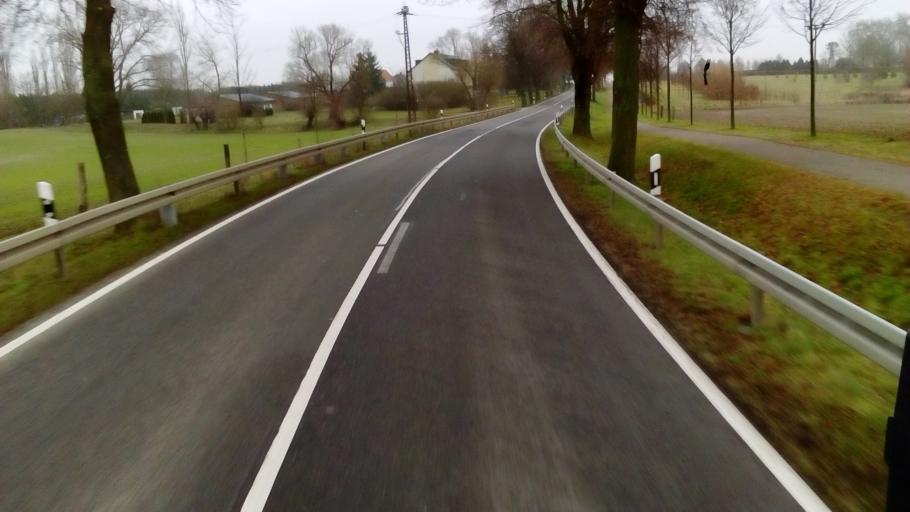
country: DE
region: Mecklenburg-Vorpommern
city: Strasburg
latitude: 53.5011
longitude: 13.7725
